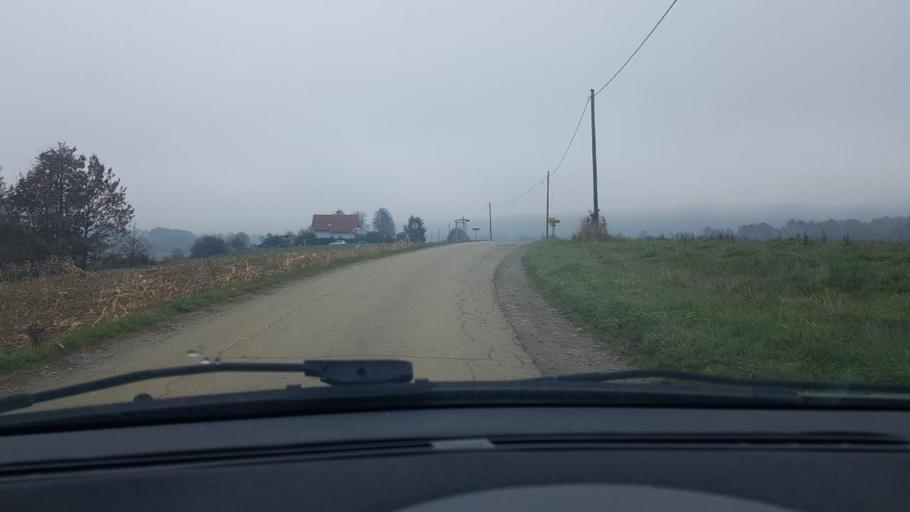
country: HR
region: Krapinsko-Zagorska
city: Zlatar
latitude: 46.1096
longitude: 16.1779
